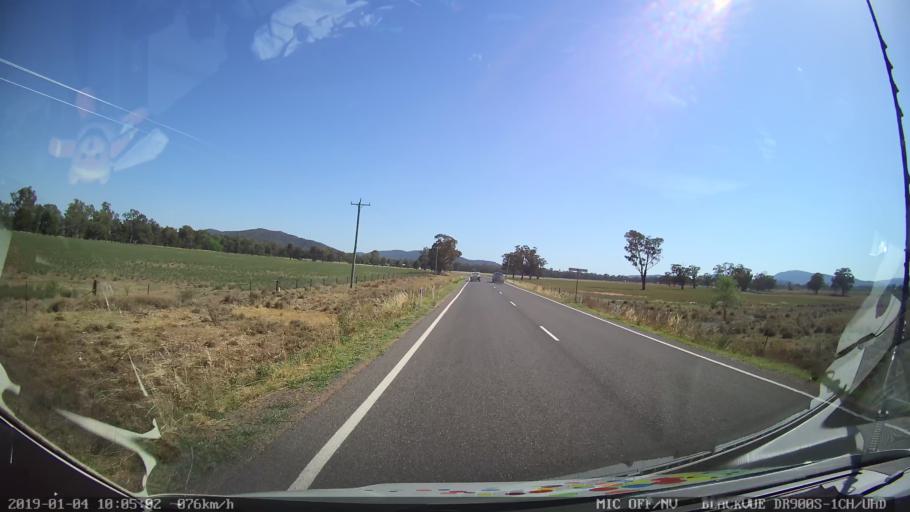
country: AU
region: New South Wales
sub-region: Cabonne
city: Canowindra
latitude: -33.4463
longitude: 148.3637
